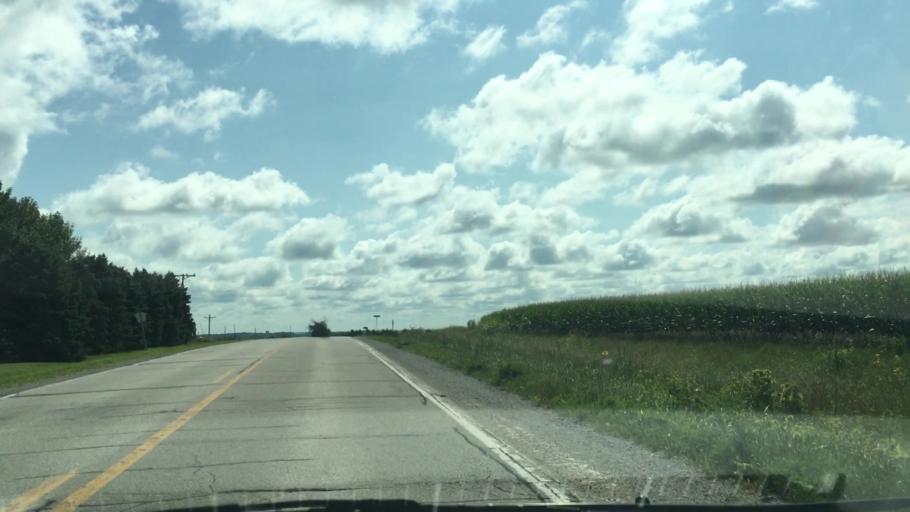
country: US
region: Iowa
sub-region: Johnson County
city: Solon
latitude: 41.8310
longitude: -91.4458
